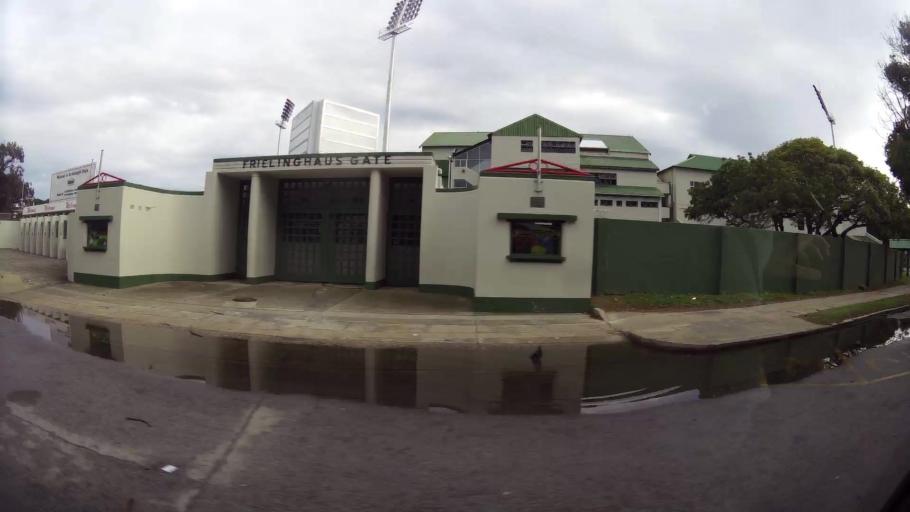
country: ZA
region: Eastern Cape
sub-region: Nelson Mandela Bay Metropolitan Municipality
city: Port Elizabeth
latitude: -33.9677
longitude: 25.6108
